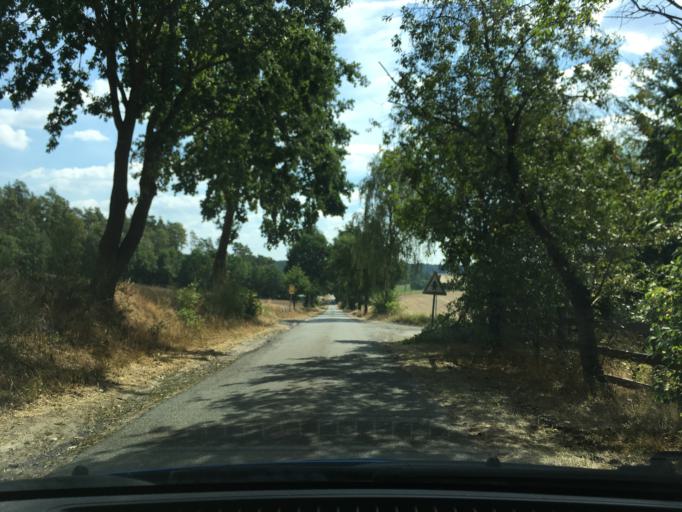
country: DE
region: Lower Saxony
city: Gohrde
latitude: 53.1221
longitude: 10.9439
